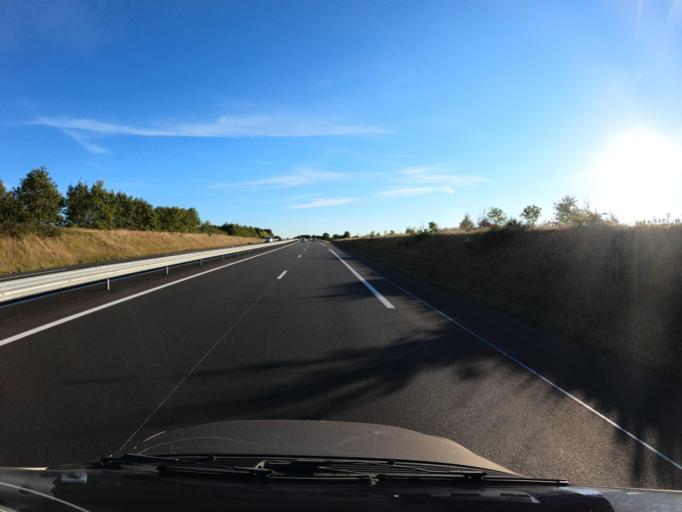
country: FR
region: Pays de la Loire
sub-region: Departement de la Vendee
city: Mortagne-sur-Sevre
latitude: 46.9841
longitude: -0.9177
